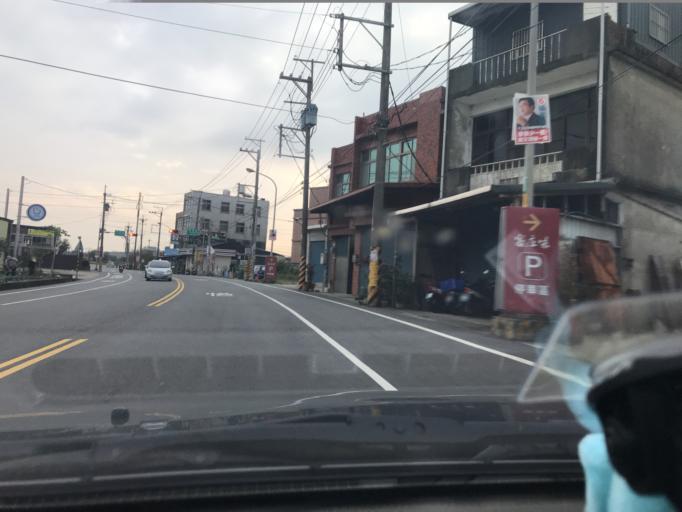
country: TW
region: Taiwan
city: Daxi
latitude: 24.8970
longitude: 121.2271
